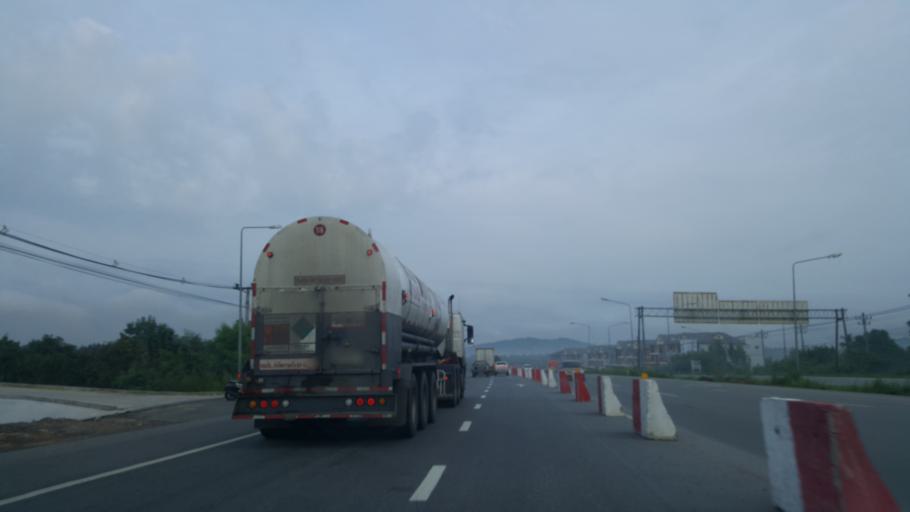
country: TH
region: Chon Buri
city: Phatthaya
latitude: 12.9145
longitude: 101.0233
